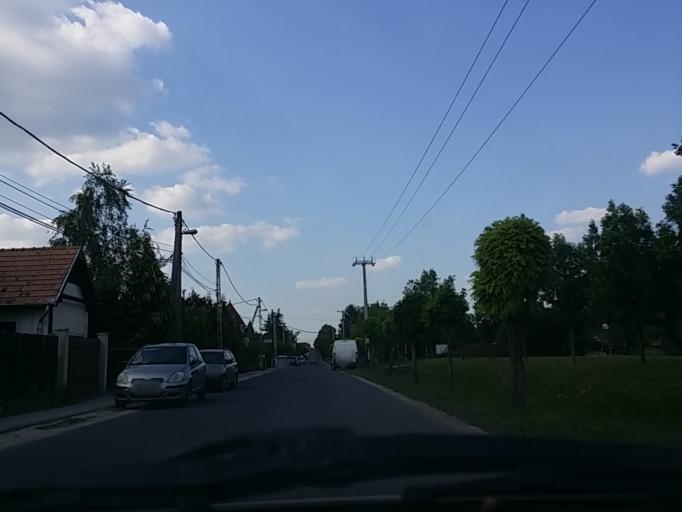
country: HU
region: Pest
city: Budakalasz
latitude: 47.6186
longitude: 19.0591
